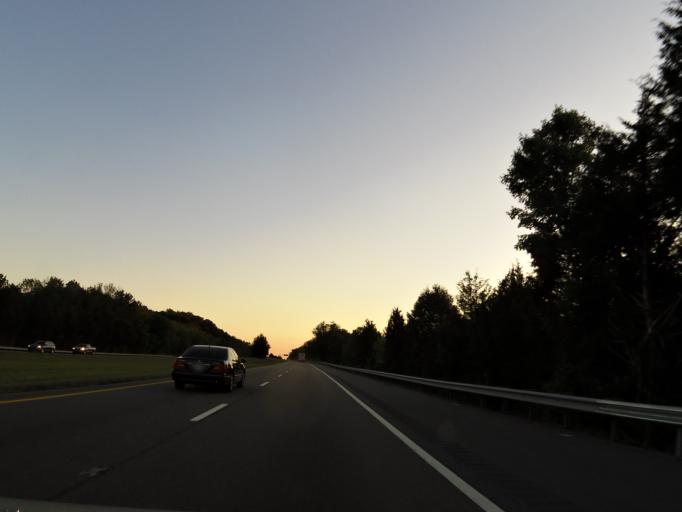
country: US
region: Tennessee
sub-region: Hamblen County
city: Morristown
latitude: 36.1890
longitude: -83.1850
